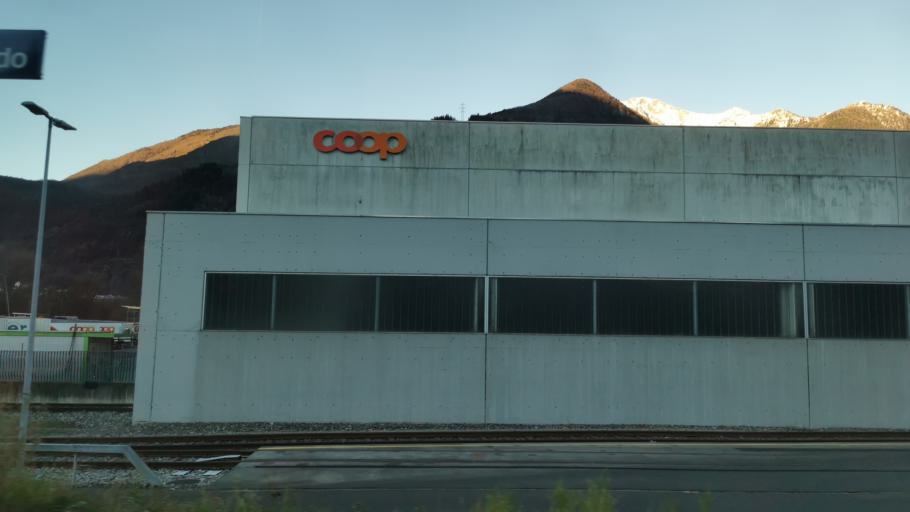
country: CH
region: Ticino
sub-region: Bellinzona District
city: Lumino
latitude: 46.2228
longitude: 9.0416
